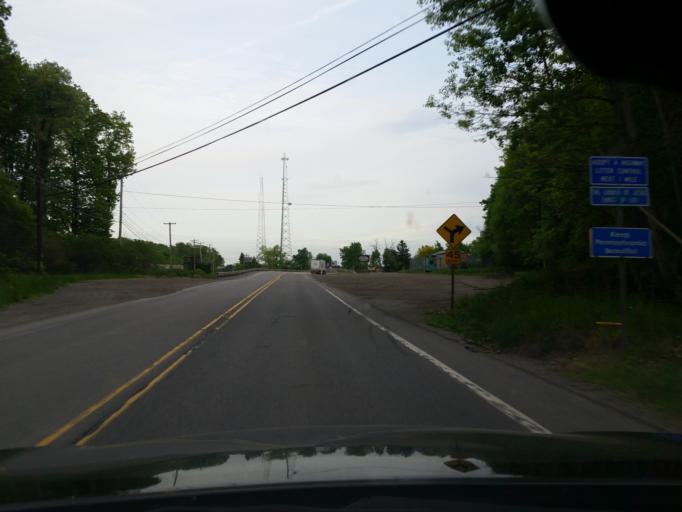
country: US
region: Pennsylvania
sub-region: Elk County
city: Ridgway
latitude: 41.3842
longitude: -78.6881
